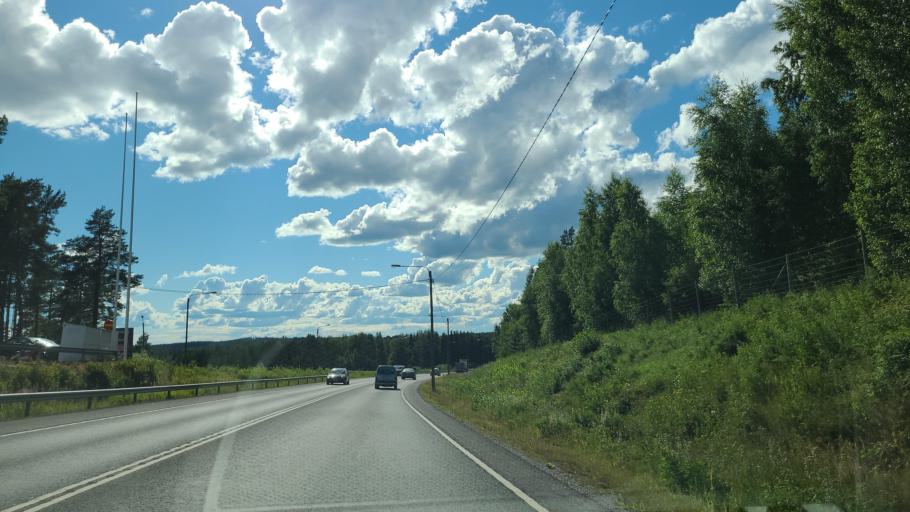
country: FI
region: Pirkanmaa
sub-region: Tampere
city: Kuhmalahti
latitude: 61.7341
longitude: 24.7743
